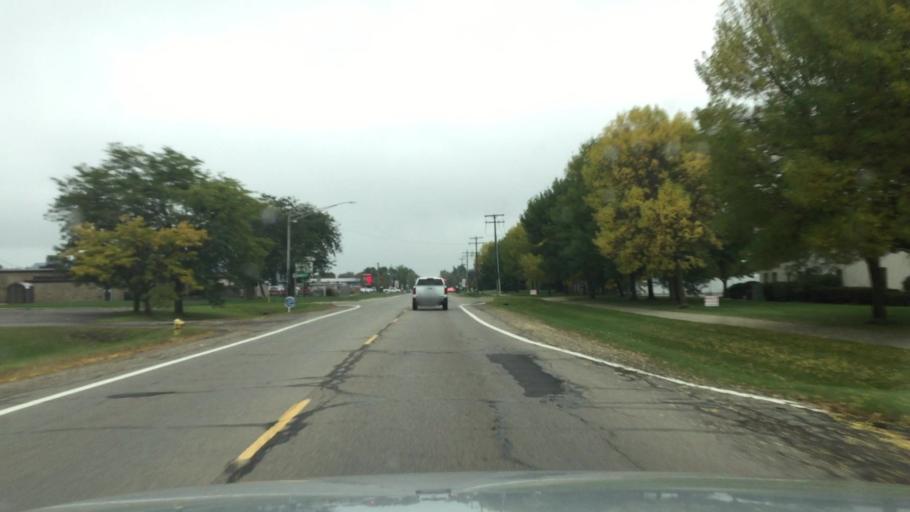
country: US
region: Michigan
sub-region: Oakland County
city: Waterford
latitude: 42.6636
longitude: -83.4062
